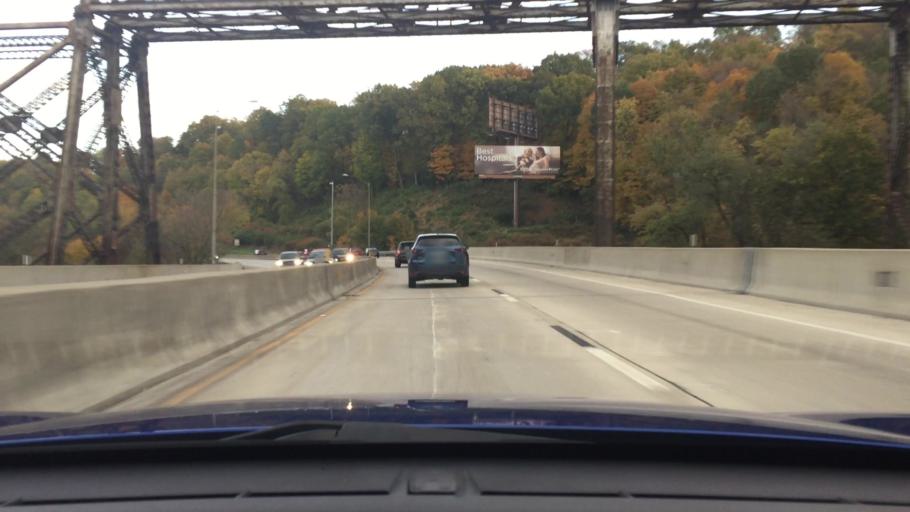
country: US
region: Pennsylvania
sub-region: Allegheny County
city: Carnegie
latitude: 40.4109
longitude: -80.0742
